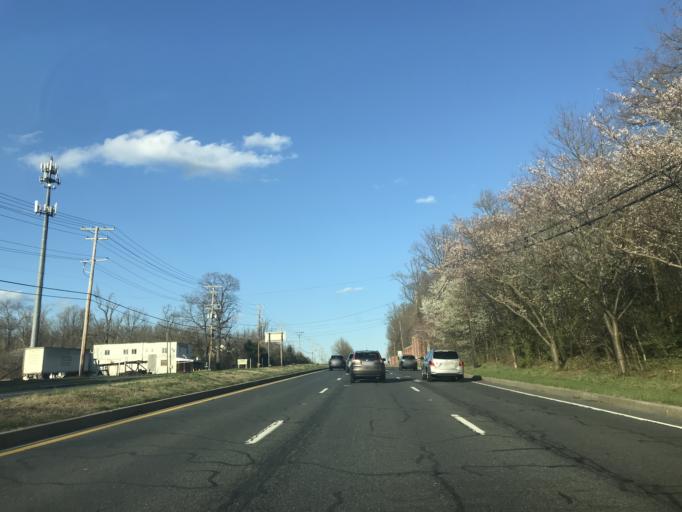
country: US
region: Maryland
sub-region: Prince George's County
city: Glenn Dale
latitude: 38.9582
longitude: -76.8041
